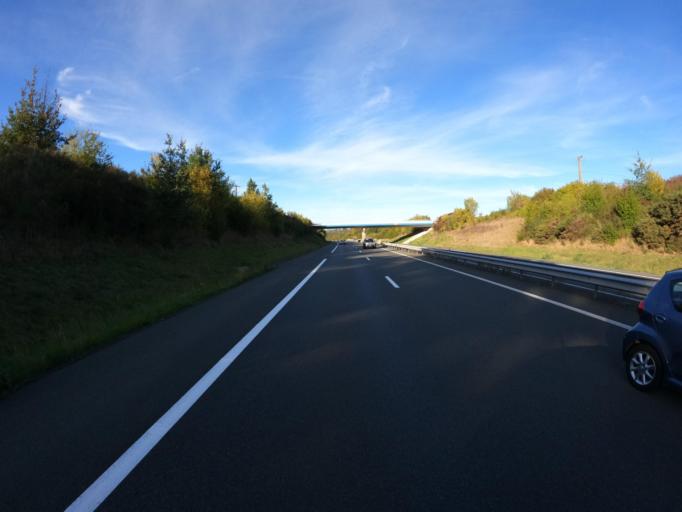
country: FR
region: Pays de la Loire
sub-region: Departement de Maine-et-Loire
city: Saint-Lambert-du-Lattay
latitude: 47.2977
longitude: -0.6101
